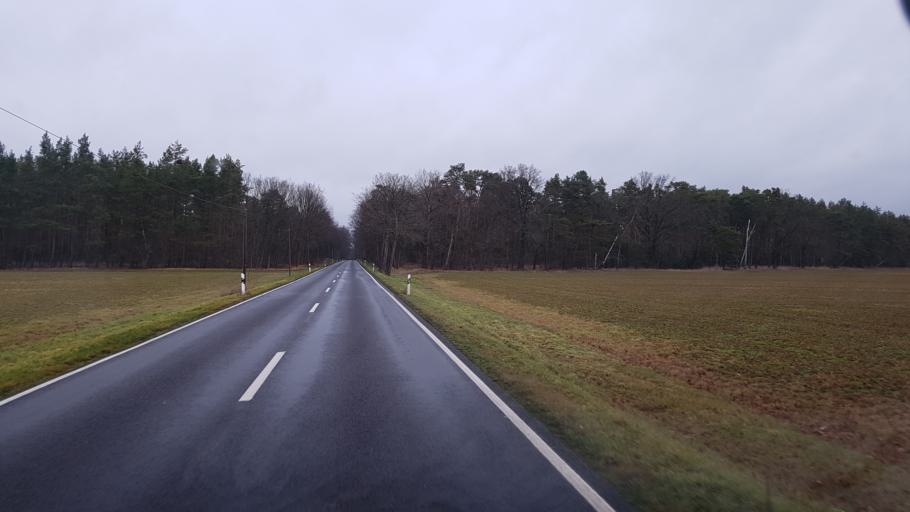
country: DE
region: Brandenburg
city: Altdobern
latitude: 51.6925
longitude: 14.0266
